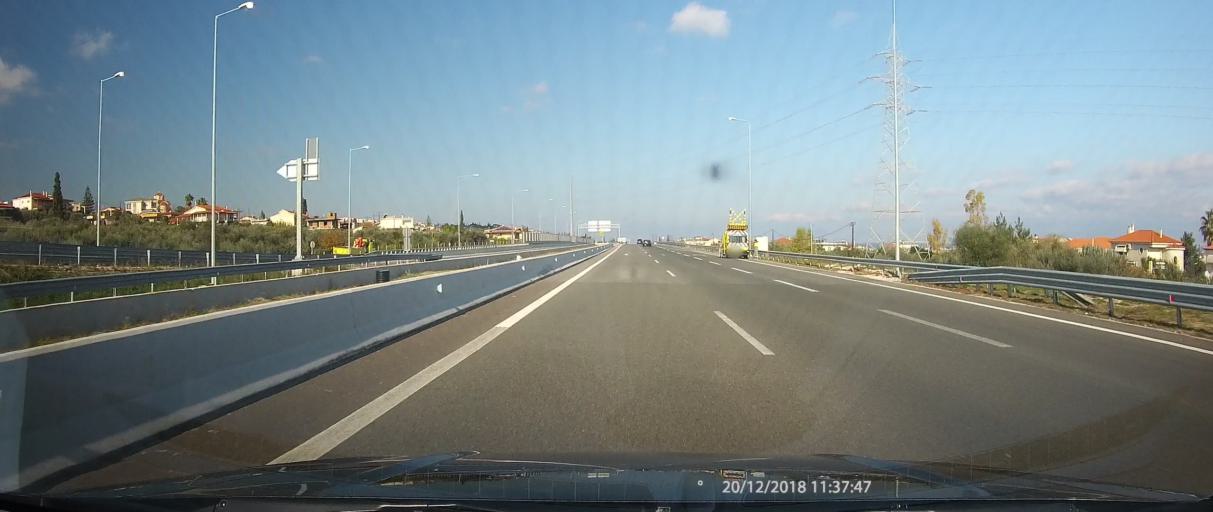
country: GR
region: Peloponnese
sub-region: Nomos Korinthias
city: Pasion
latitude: 38.0112
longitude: 22.7333
